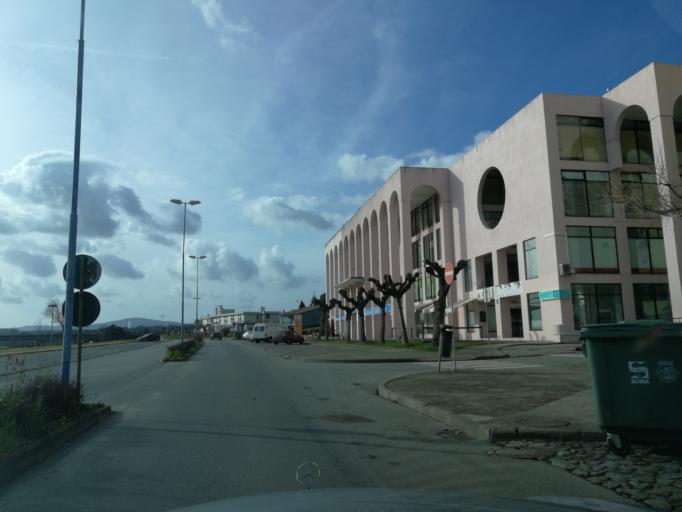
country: PT
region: Viana do Castelo
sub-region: Valenca
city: Valenca
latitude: 42.0229
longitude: -8.6440
